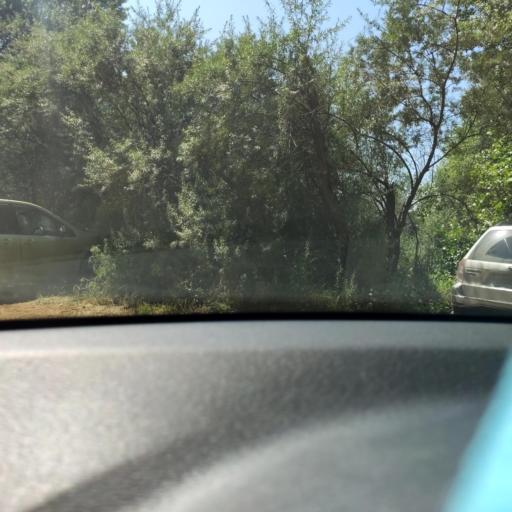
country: RU
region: Samara
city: Smyshlyayevka
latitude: 53.2194
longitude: 50.3437
